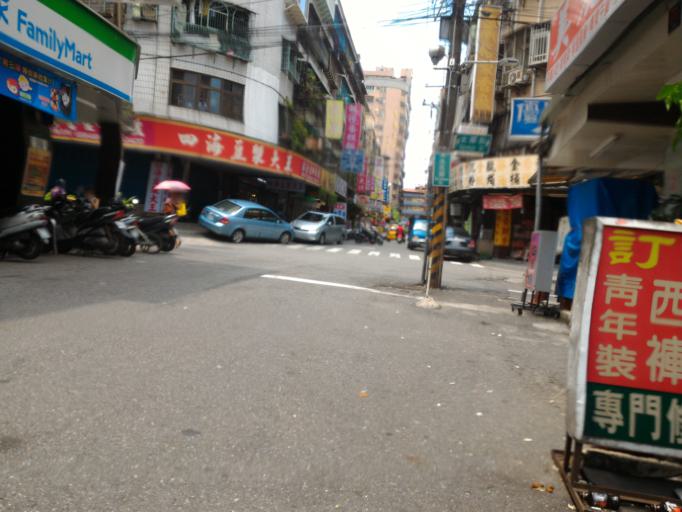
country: TW
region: Taipei
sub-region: Taipei
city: Banqiao
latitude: 24.9795
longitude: 121.4186
